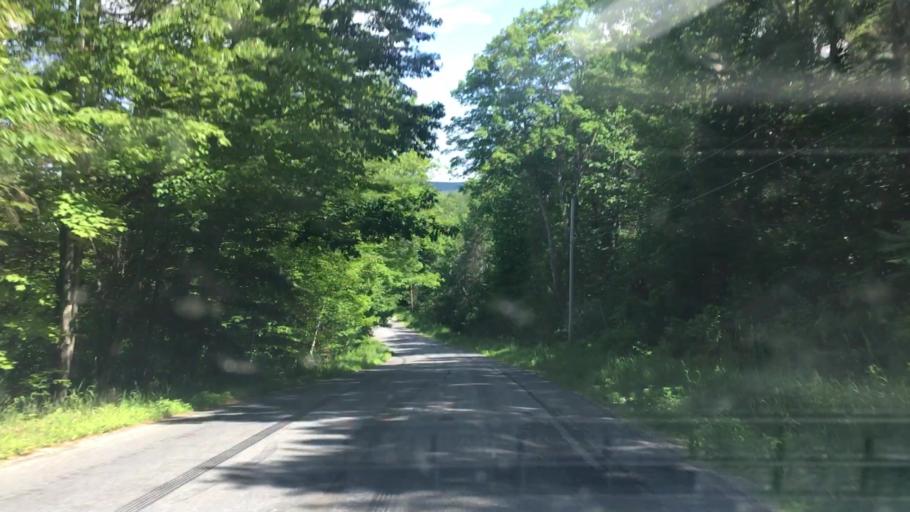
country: US
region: Maine
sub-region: Franklin County
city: Chesterville
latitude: 44.5562
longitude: -70.1129
